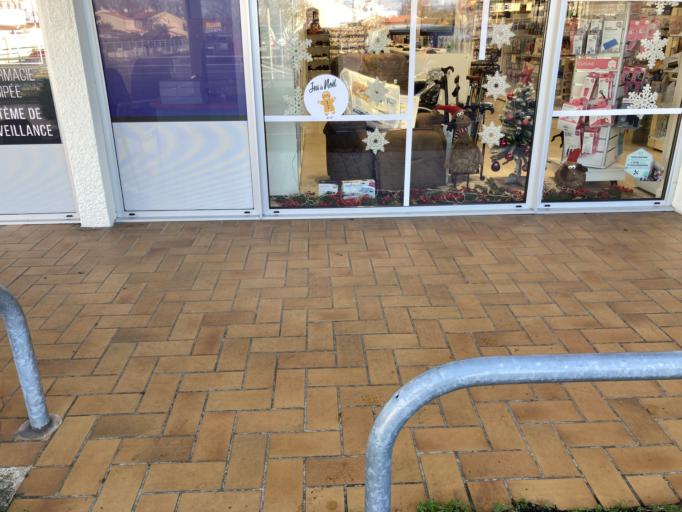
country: FR
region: Pays de la Loire
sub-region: Departement de la Loire-Atlantique
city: Saint-Sebastien-sur-Loire
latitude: 47.2035
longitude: -1.4912
